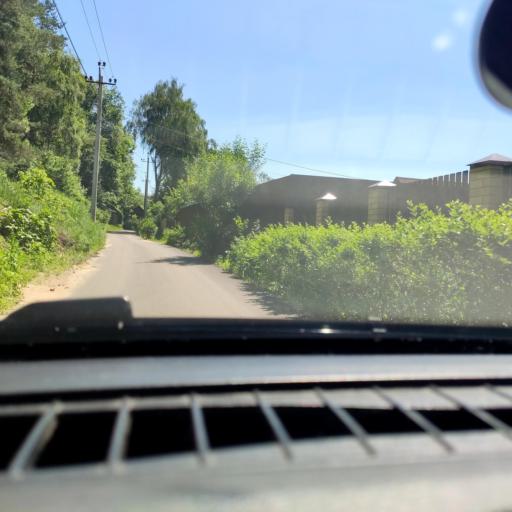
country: RU
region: Voronezj
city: Podgornoye
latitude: 51.7901
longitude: 39.1348
